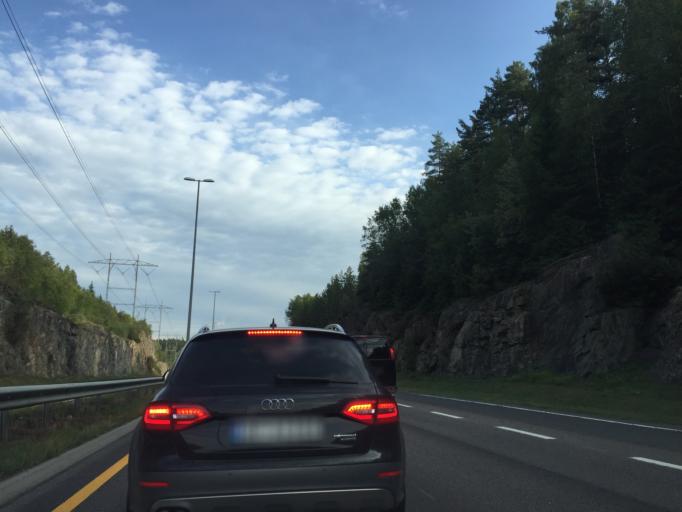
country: NO
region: Akershus
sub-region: Oppegard
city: Kolbotn
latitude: 59.8280
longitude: 10.8435
